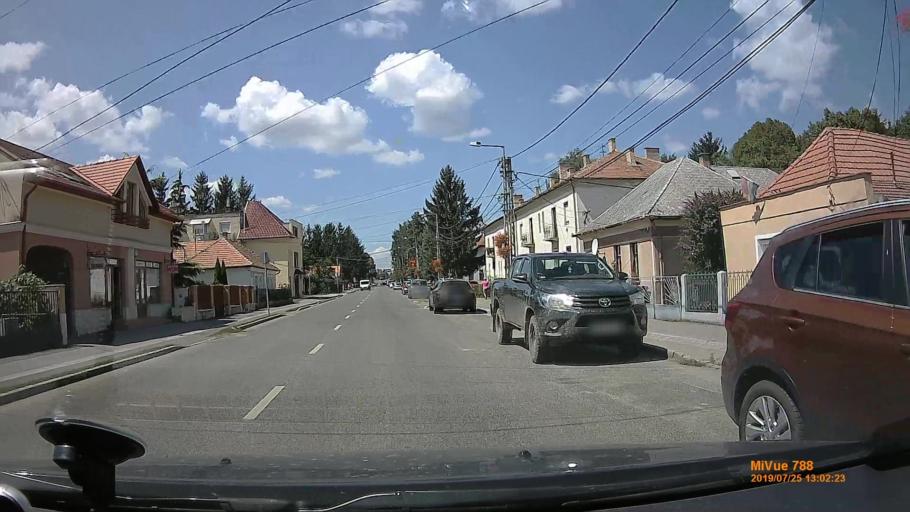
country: HU
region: Borsod-Abauj-Zemplen
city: Encs
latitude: 48.3322
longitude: 21.1176
